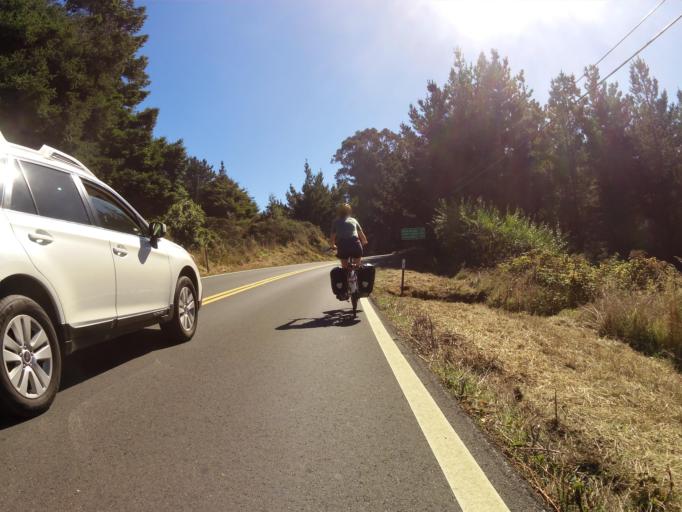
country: US
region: California
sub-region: Mendocino County
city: Fort Bragg
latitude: 39.6292
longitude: -123.7824
